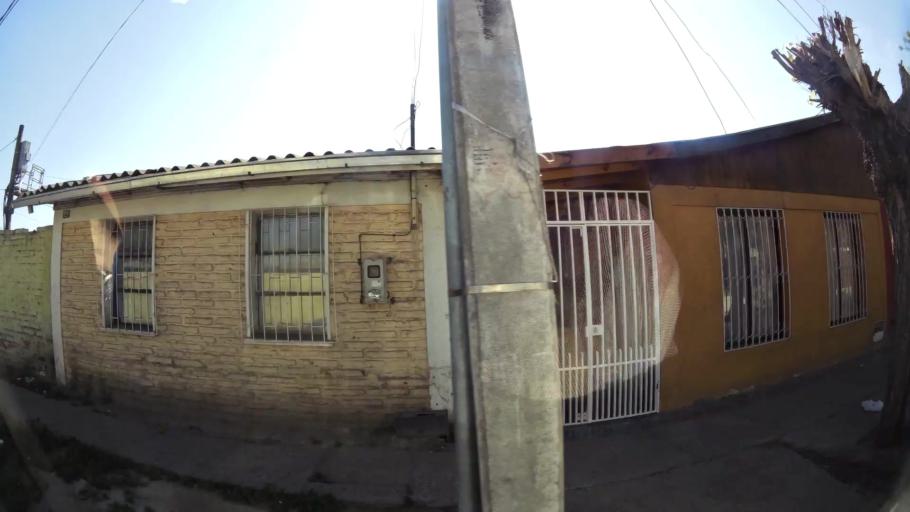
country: CL
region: Santiago Metropolitan
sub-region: Provincia de Maipo
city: San Bernardo
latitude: -33.5174
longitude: -70.6995
